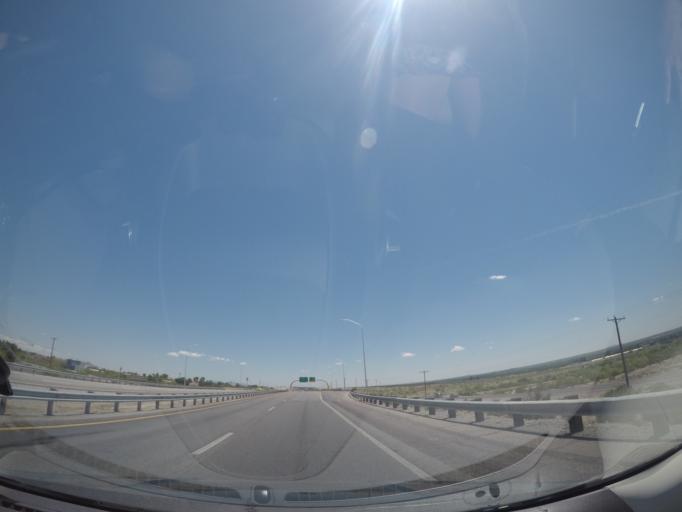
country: US
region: New Mexico
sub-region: Dona Ana County
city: University Park
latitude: 32.2698
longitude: -106.7331
